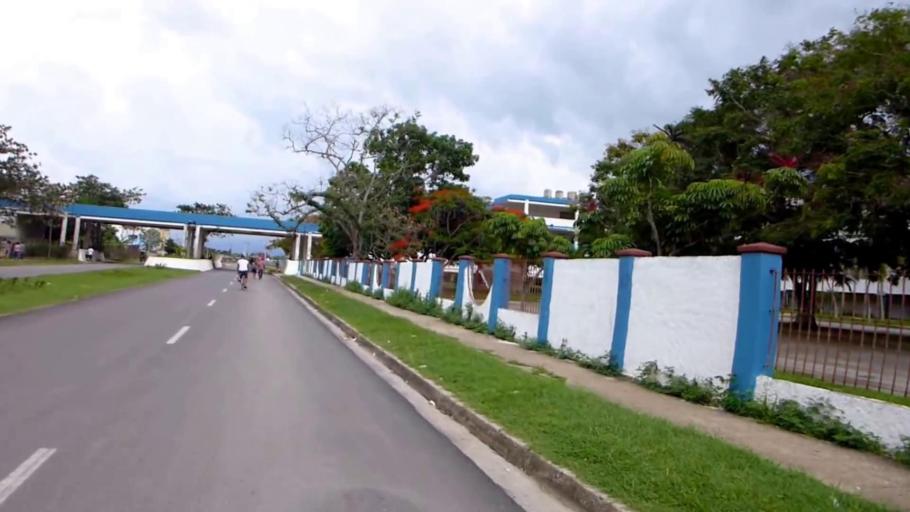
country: CU
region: Camaguey
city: Camaguey
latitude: 21.3591
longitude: -77.8932
